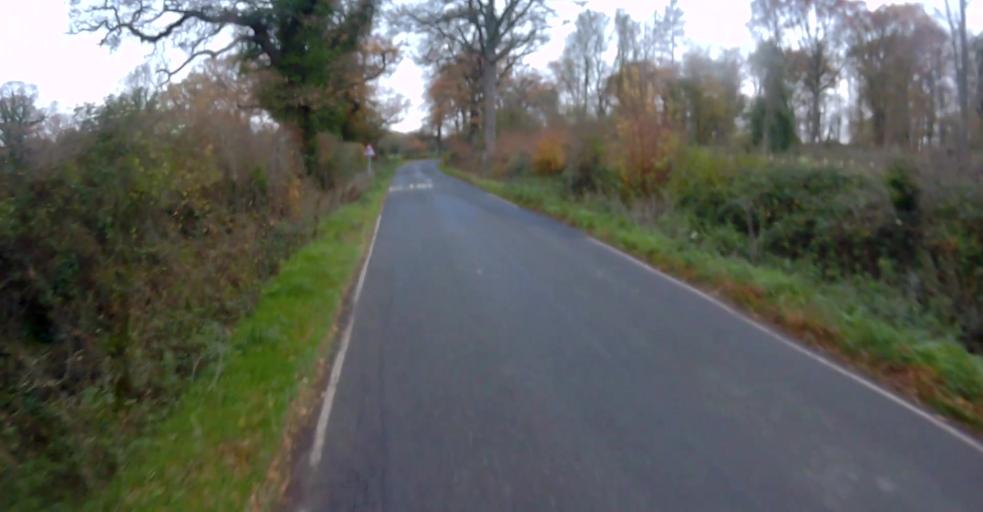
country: GB
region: England
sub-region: Wokingham
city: Swallowfield
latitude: 51.3828
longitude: -0.9360
